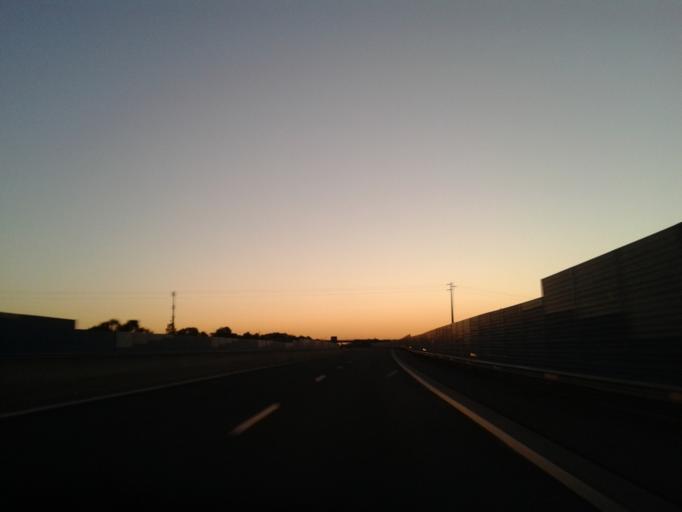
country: PT
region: Faro
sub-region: Albufeira
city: Guia
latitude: 37.1391
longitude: -8.2781
